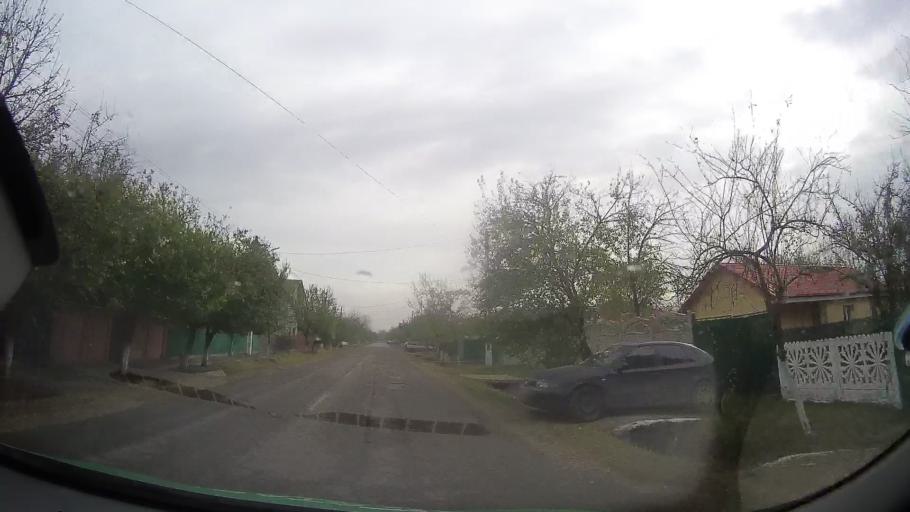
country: RO
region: Prahova
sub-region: Comuna Dumbrava
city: Dumbrava
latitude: 44.8673
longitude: 26.1988
